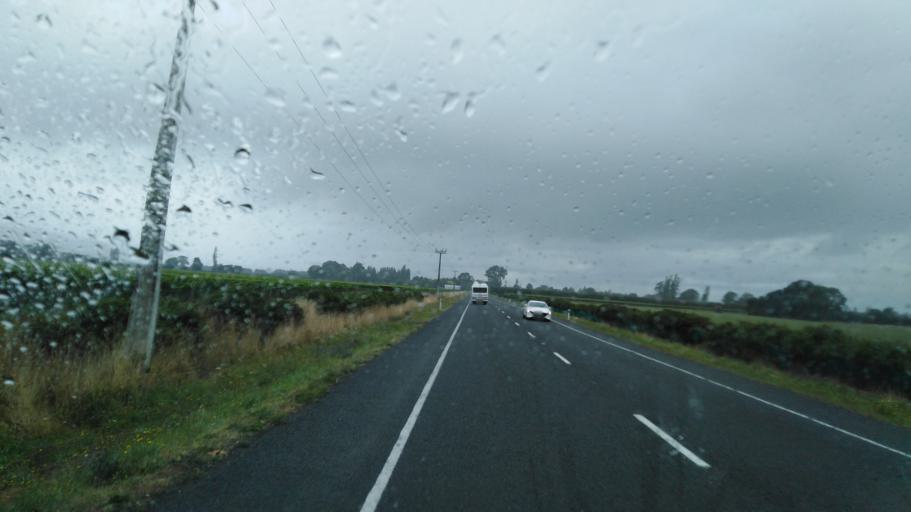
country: NZ
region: Marlborough
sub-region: Marlborough District
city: Blenheim
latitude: -41.4615
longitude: 173.9381
